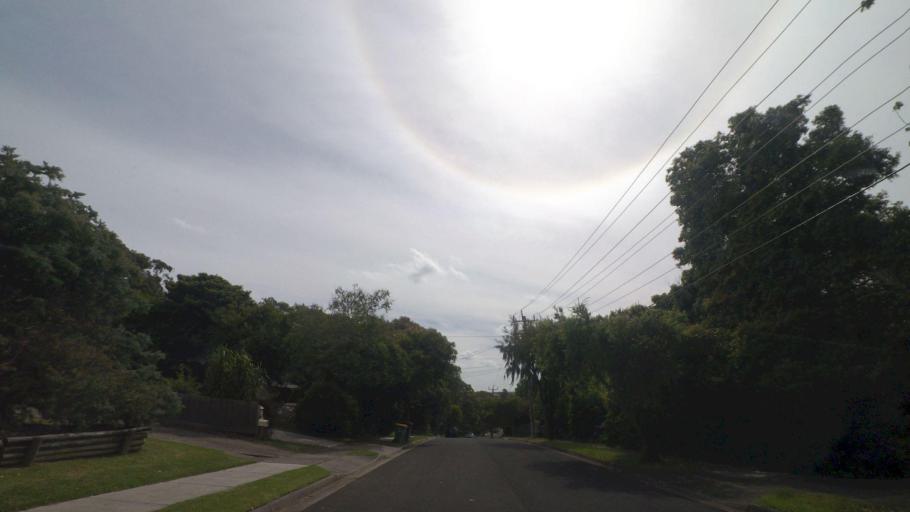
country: AU
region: Victoria
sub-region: Maroondah
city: Bayswater North
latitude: -37.8427
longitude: 145.2902
